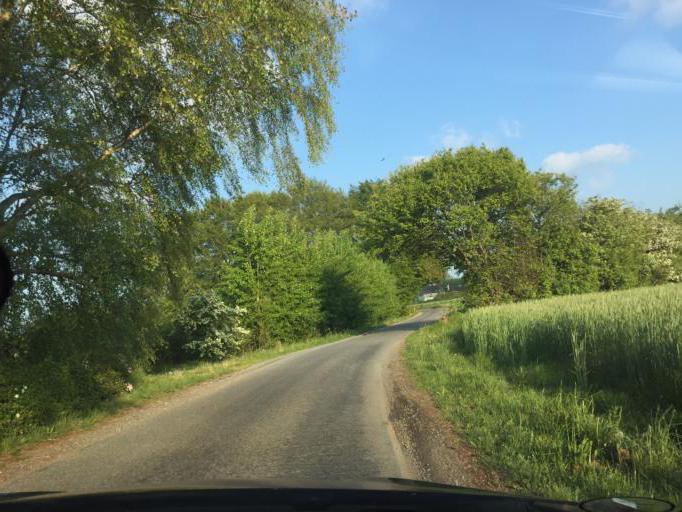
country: DK
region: South Denmark
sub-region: Odense Kommune
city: Bellinge
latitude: 55.3856
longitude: 10.2866
